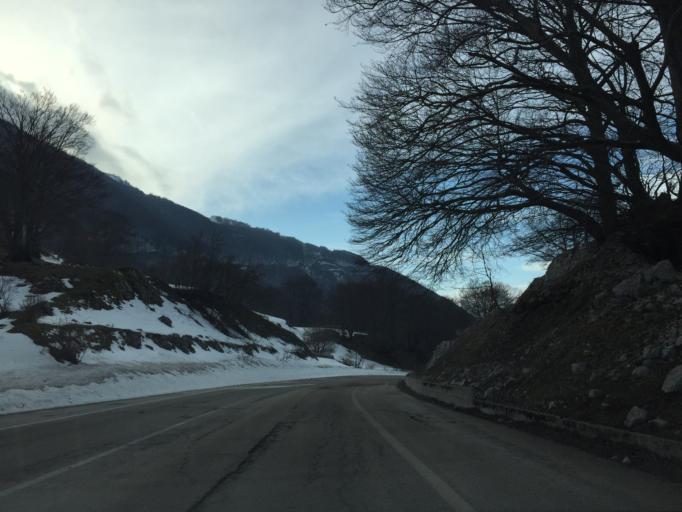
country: IT
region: Molise
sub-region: Provincia di Campobasso
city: San Massimo
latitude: 41.4682
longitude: 14.4156
